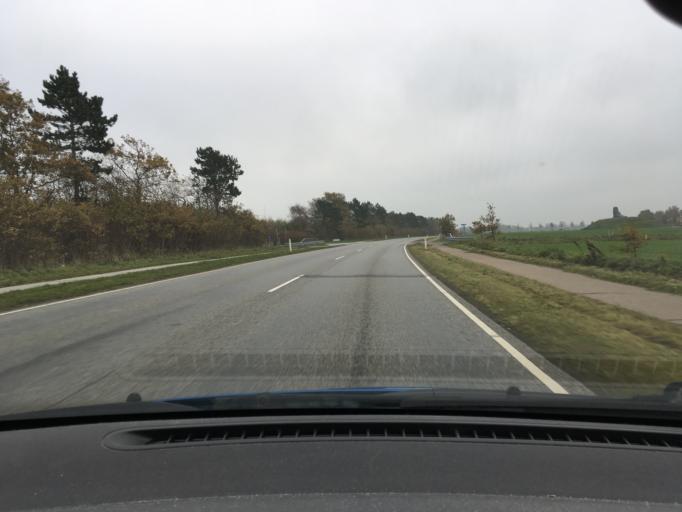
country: DK
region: South Denmark
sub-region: Tonder Kommune
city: Tonder
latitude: 54.9378
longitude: 8.8456
